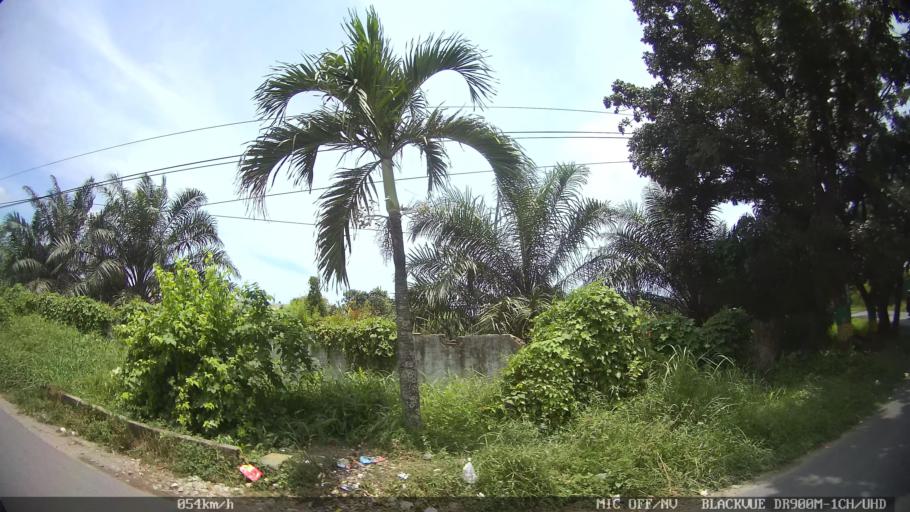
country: ID
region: North Sumatra
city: Labuhan Deli
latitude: 3.7096
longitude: 98.6664
